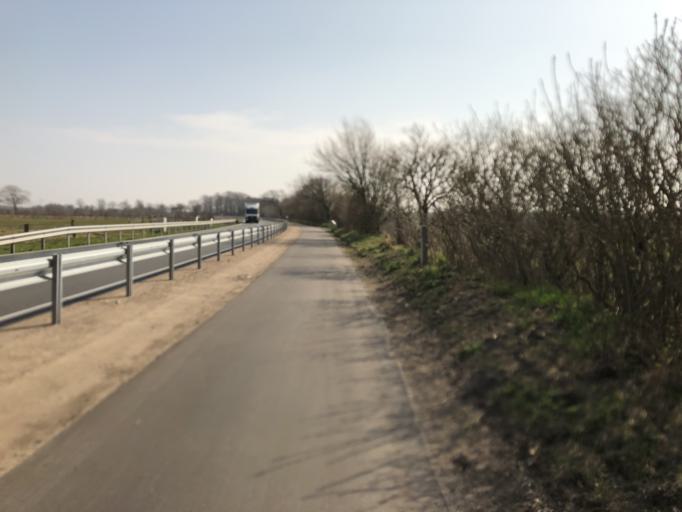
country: DE
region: Schleswig-Holstein
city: Wanderup
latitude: 54.6814
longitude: 9.3617
